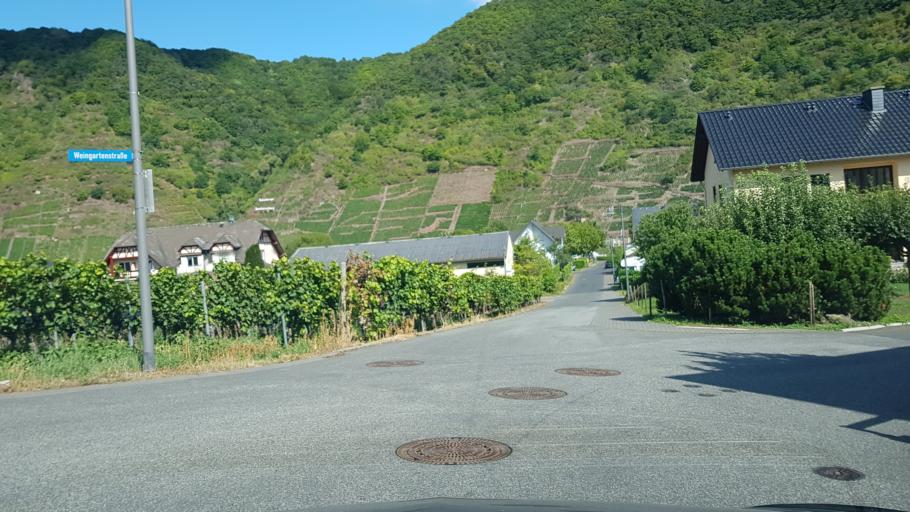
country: DE
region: Rheinland-Pfalz
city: Mesenich
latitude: 50.1096
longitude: 7.2074
